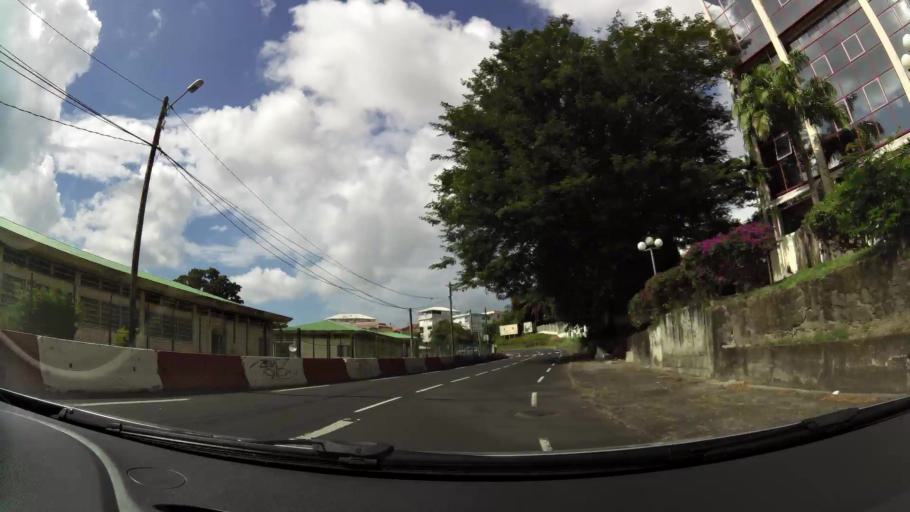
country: MQ
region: Martinique
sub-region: Martinique
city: Fort-de-France
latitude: 14.6040
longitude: -61.0800
